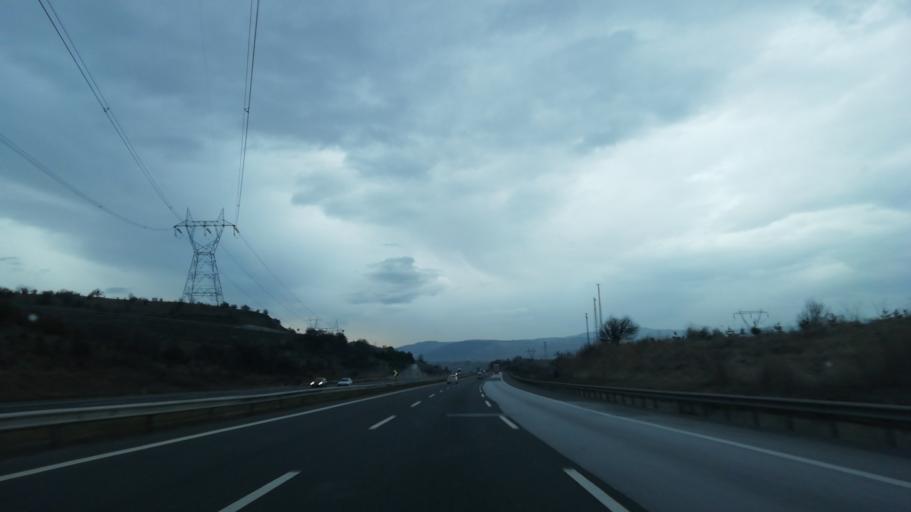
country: TR
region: Bolu
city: Yenicaga
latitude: 40.7648
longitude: 32.0395
